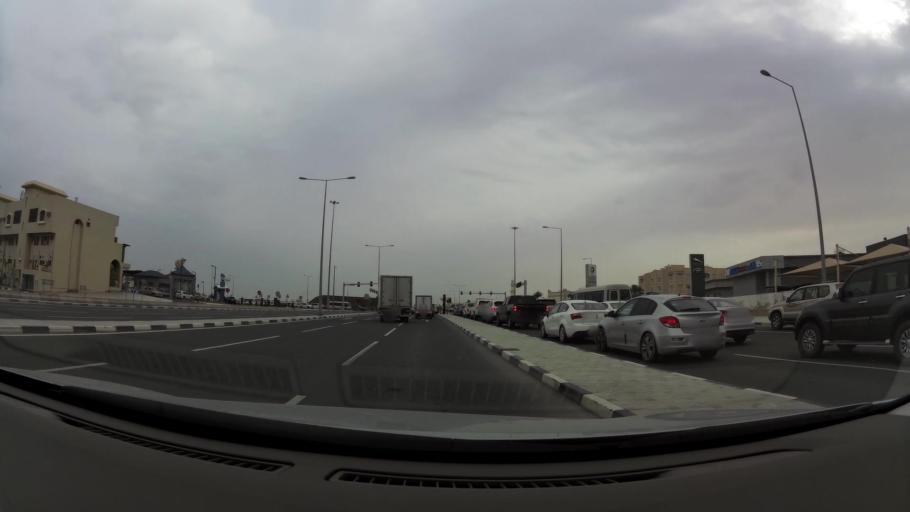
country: QA
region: Baladiyat ad Dawhah
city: Doha
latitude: 25.3233
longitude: 51.4864
